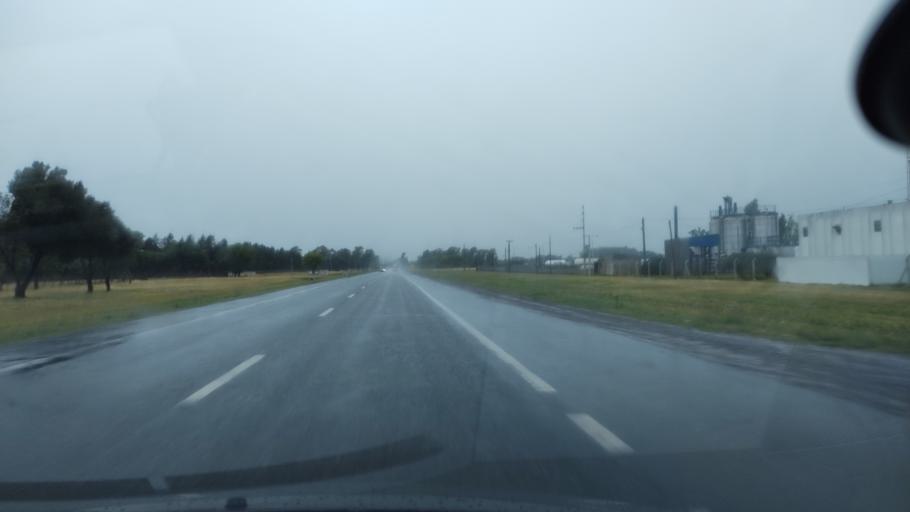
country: AR
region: Buenos Aires
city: Canuelas
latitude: -35.0571
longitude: -58.7925
